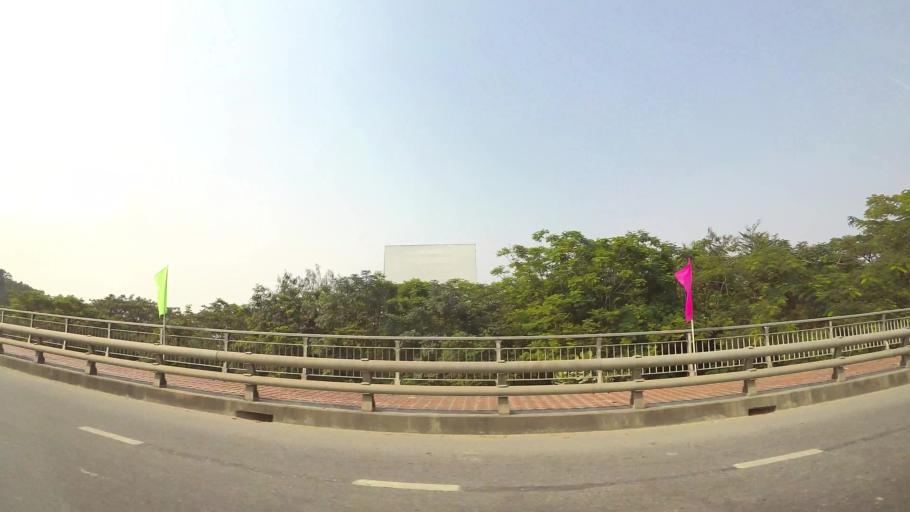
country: VN
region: Da Nang
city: Cam Le
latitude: 16.0142
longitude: 108.1933
